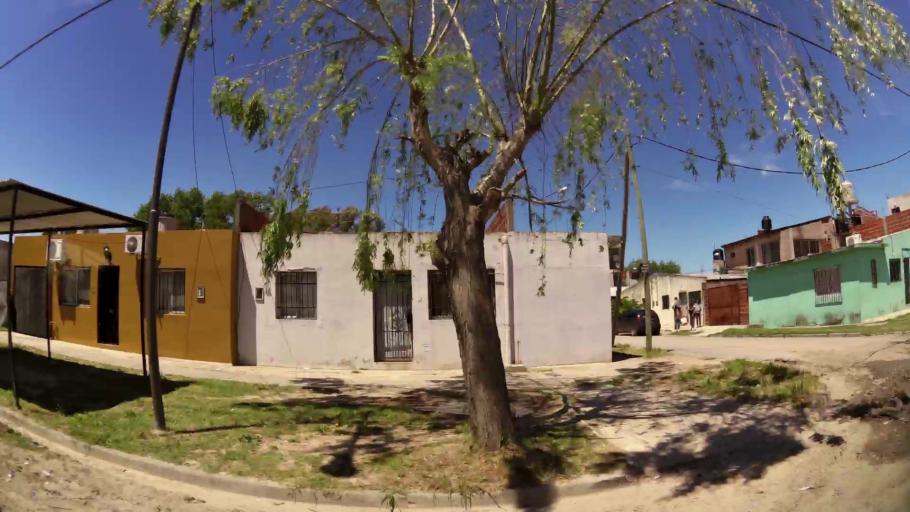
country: AR
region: Buenos Aires
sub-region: Partido de Quilmes
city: Quilmes
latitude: -34.7139
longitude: -58.3148
